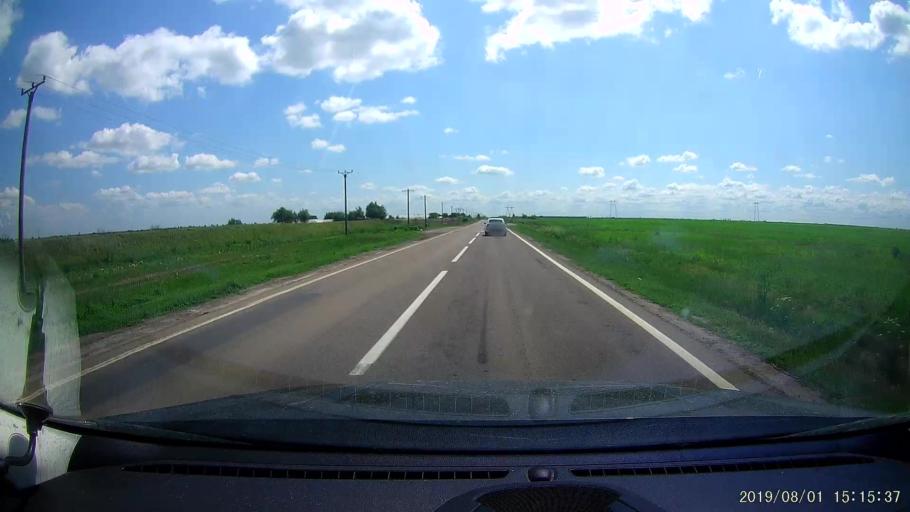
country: RO
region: Braila
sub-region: Comuna Tichilesti
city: Tichilesti
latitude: 45.1612
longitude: 27.8655
